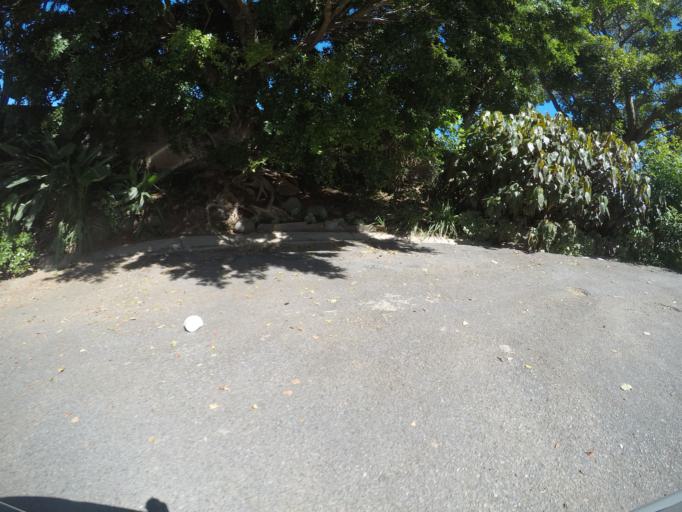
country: ZA
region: Eastern Cape
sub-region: Buffalo City Metropolitan Municipality
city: East London
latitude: -32.9842
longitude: 27.9298
